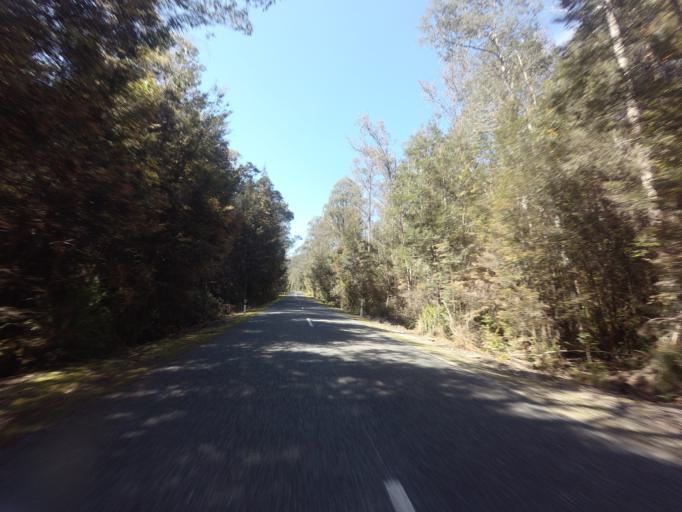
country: AU
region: Tasmania
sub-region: Derwent Valley
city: New Norfolk
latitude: -42.7384
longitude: 146.4217
